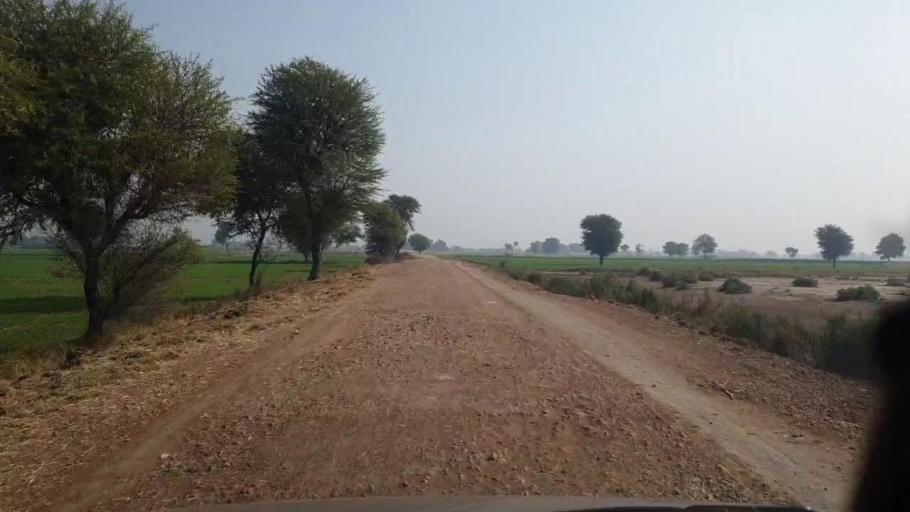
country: PK
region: Sindh
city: Shahdadpur
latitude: 26.0383
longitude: 68.4986
